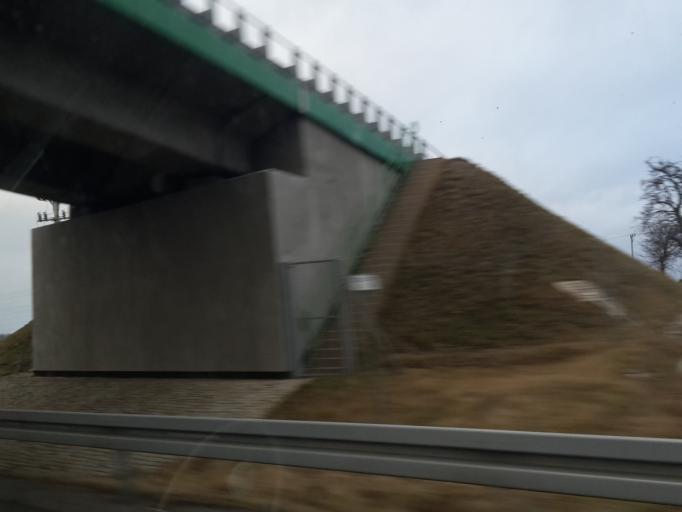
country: PL
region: Warmian-Masurian Voivodeship
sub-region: Powiat ostrodzki
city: Maldyty
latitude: 53.8440
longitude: 19.7548
